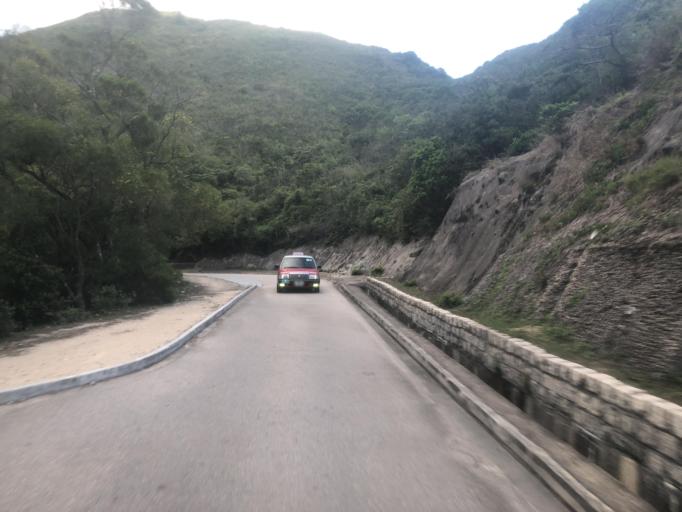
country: HK
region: Sai Kung
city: Sai Kung
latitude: 22.3648
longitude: 114.3476
